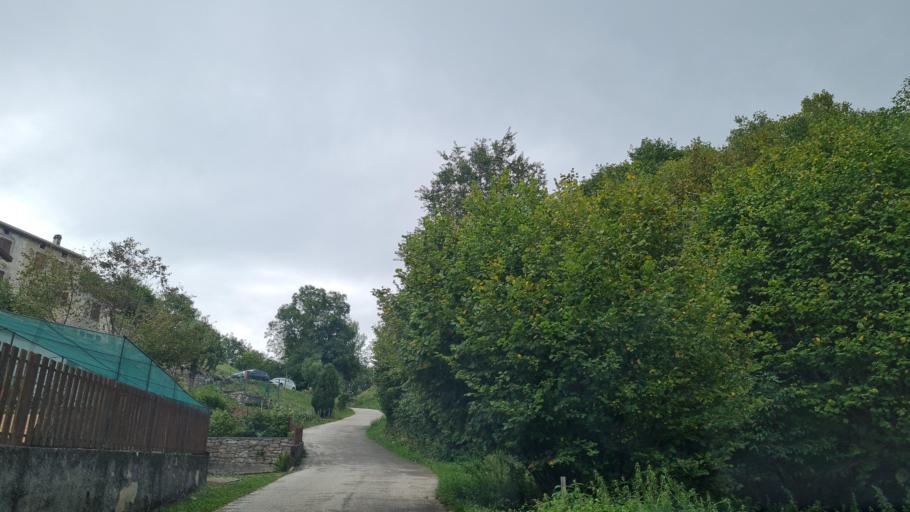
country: IT
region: Veneto
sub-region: Provincia di Vicenza
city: Marostica
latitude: 45.7953
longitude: 11.6608
